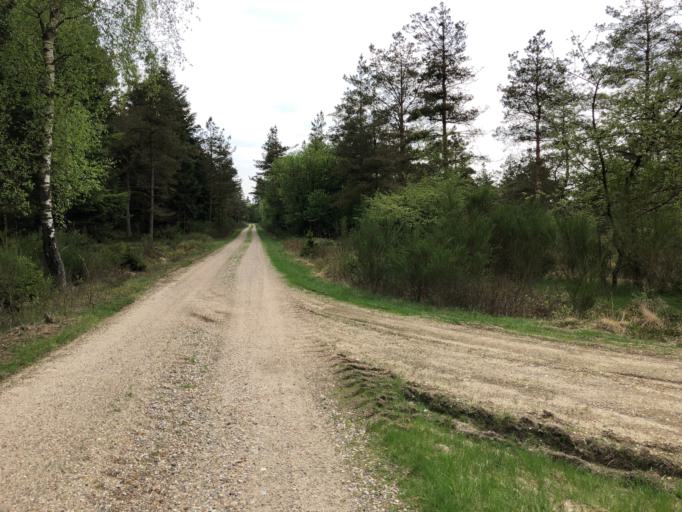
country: DK
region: Central Jutland
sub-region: Holstebro Kommune
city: Ulfborg
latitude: 56.2879
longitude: 8.4325
